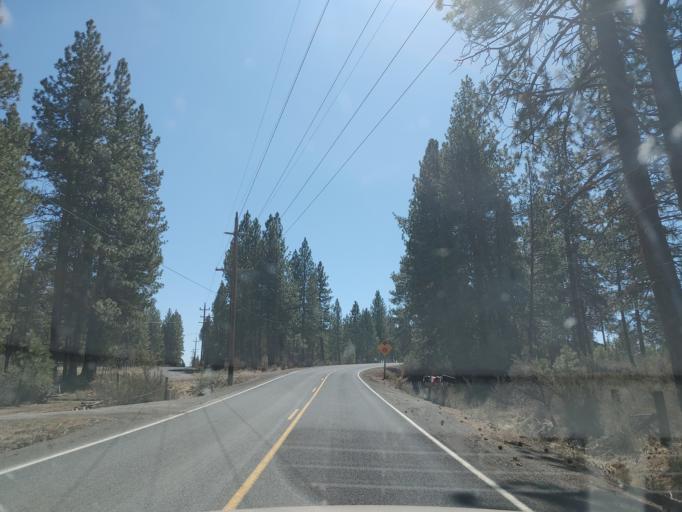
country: US
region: Oregon
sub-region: Klamath County
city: Klamath Falls
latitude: 42.5502
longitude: -121.8966
